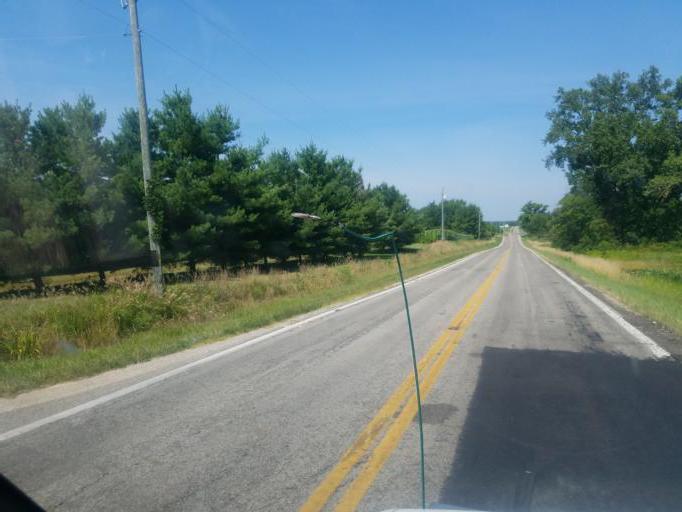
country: US
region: Ohio
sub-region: Champaign County
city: North Lewisburg
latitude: 40.2278
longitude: -83.4945
